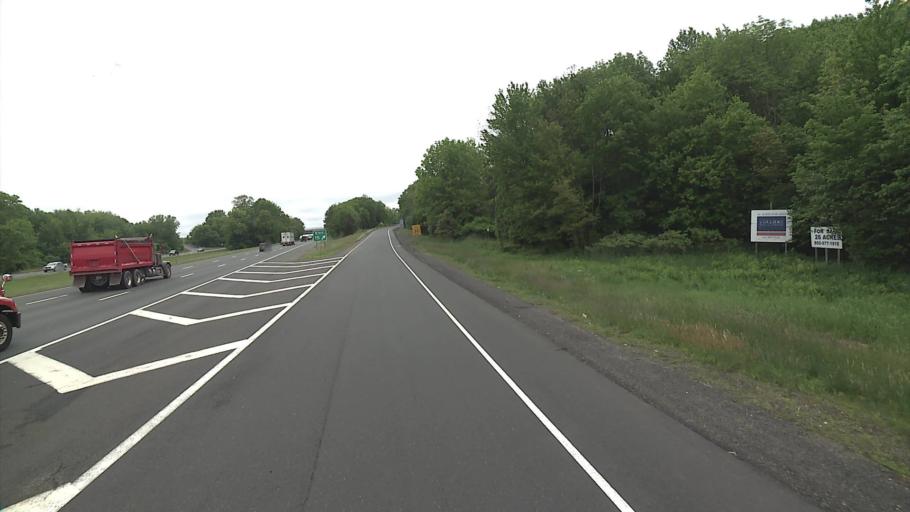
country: US
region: Connecticut
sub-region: New Haven County
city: Wallingford Center
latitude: 41.4767
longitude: -72.7708
